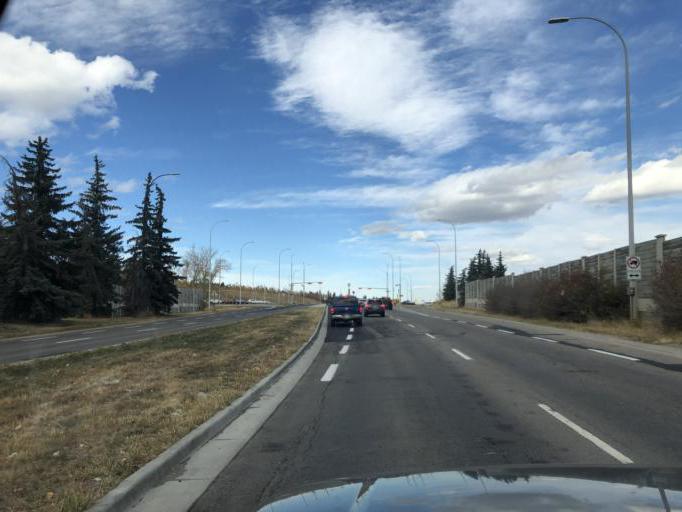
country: CA
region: Alberta
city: Calgary
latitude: 50.9597
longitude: -114.0947
